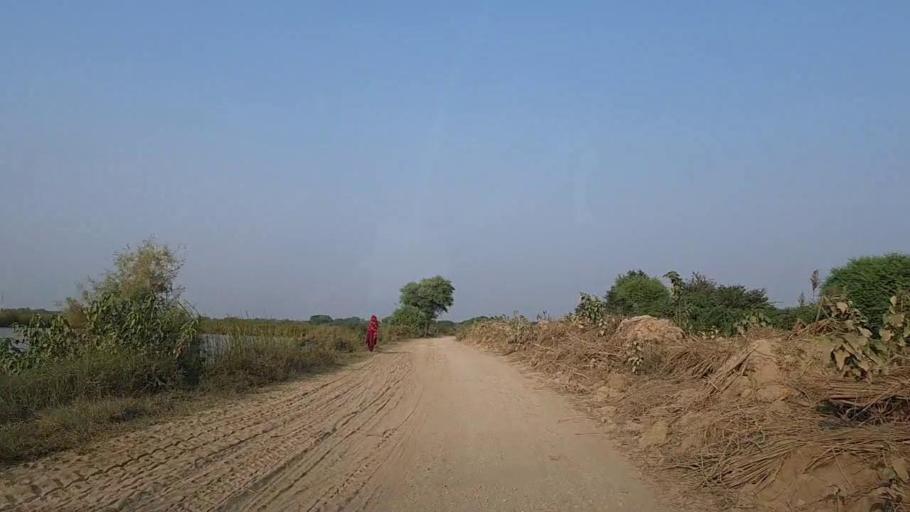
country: PK
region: Sindh
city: Thatta
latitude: 24.6845
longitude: 67.7888
